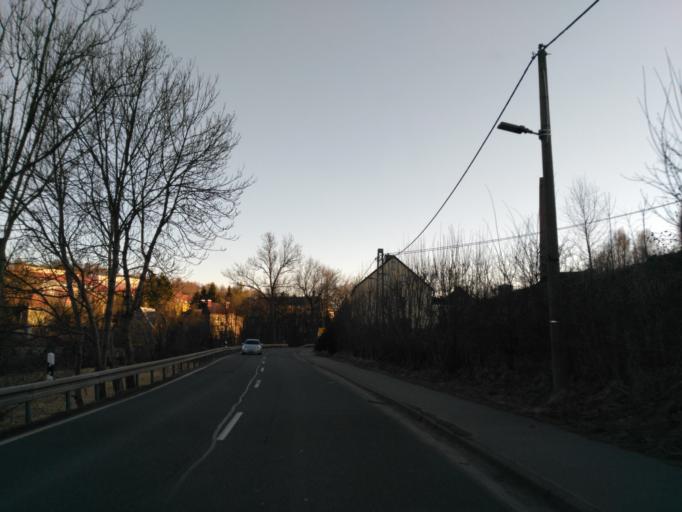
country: CZ
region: Ustecky
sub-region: Okres Chomutov
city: Vejprty
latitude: 50.4946
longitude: 13.0274
